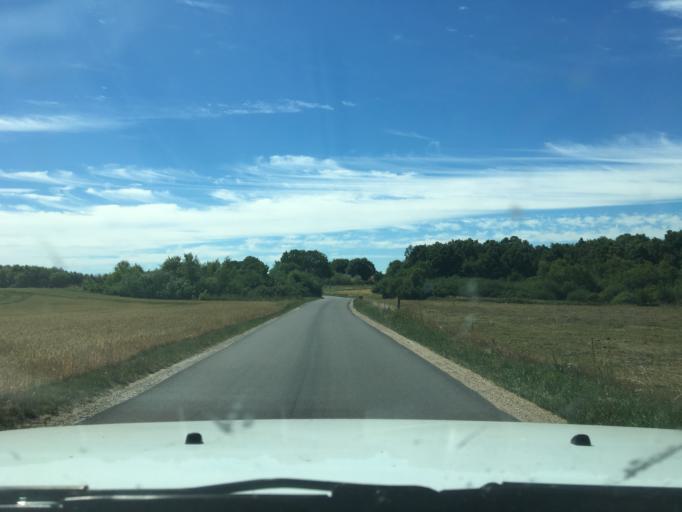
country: DK
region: Central Jutland
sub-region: Syddjurs Kommune
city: Ryomgard
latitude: 56.4326
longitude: 10.5686
